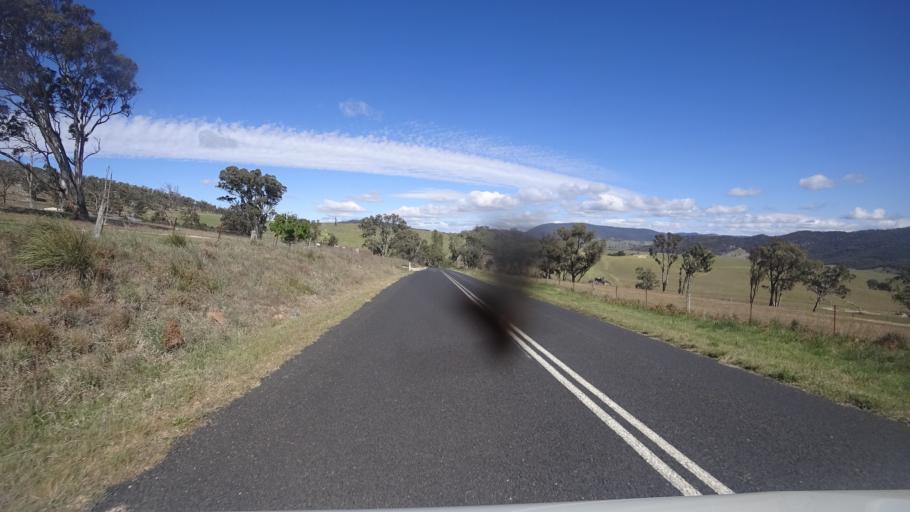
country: AU
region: New South Wales
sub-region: Lithgow
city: Bowenfels
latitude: -33.5212
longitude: 149.9729
